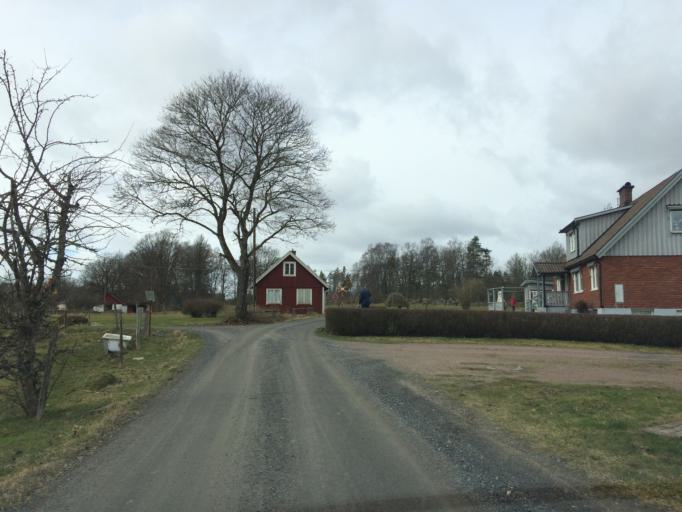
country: SE
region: Skane
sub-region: Osby Kommun
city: Lonsboda
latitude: 56.4082
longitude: 14.3221
